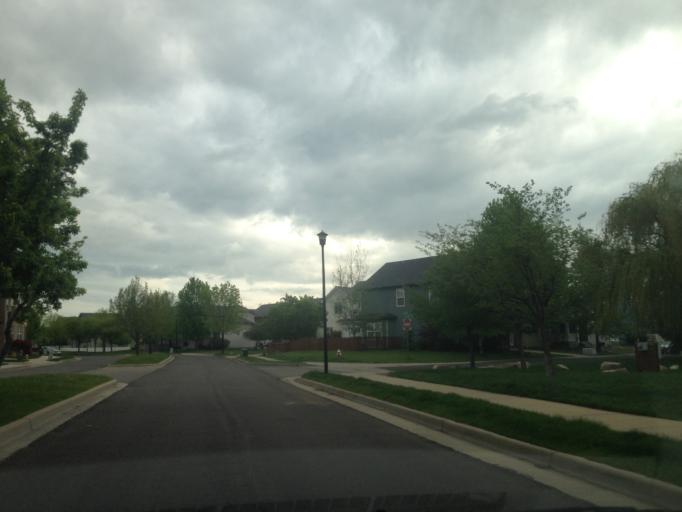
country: US
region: Colorado
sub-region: Boulder County
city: Longmont
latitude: 40.1435
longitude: -105.0992
